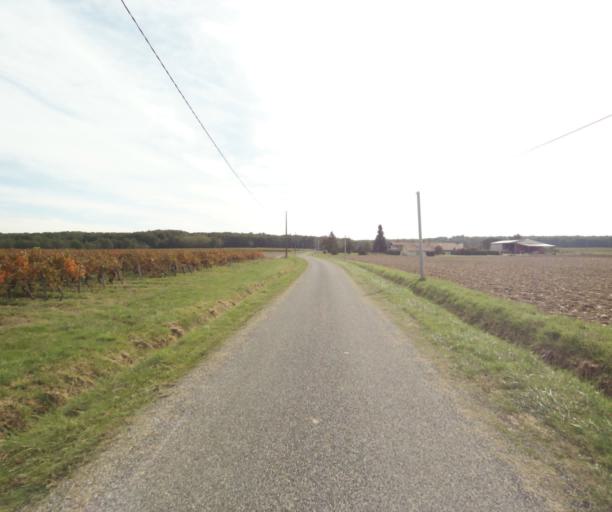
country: FR
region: Midi-Pyrenees
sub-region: Departement du Tarn-et-Garonne
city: Campsas
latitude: 43.8787
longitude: 1.3601
